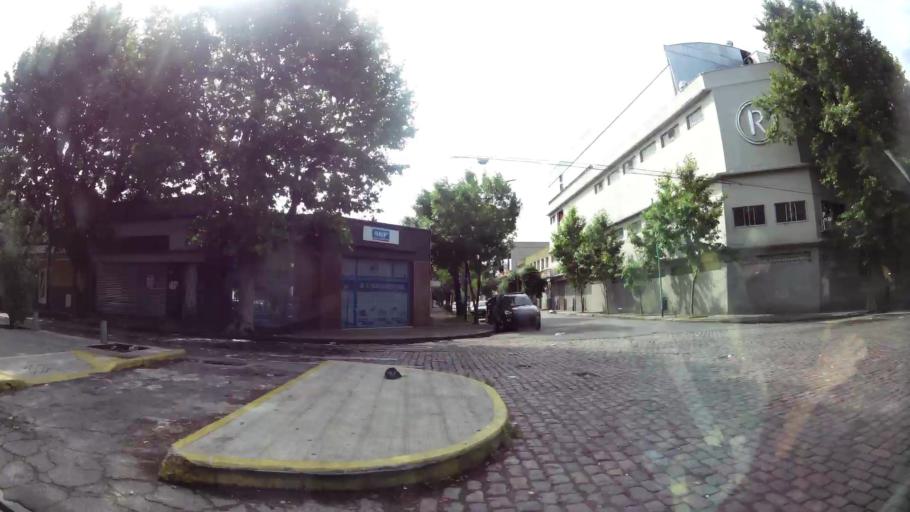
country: AR
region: Buenos Aires F.D.
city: Villa Lugano
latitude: -34.6639
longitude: -58.5018
